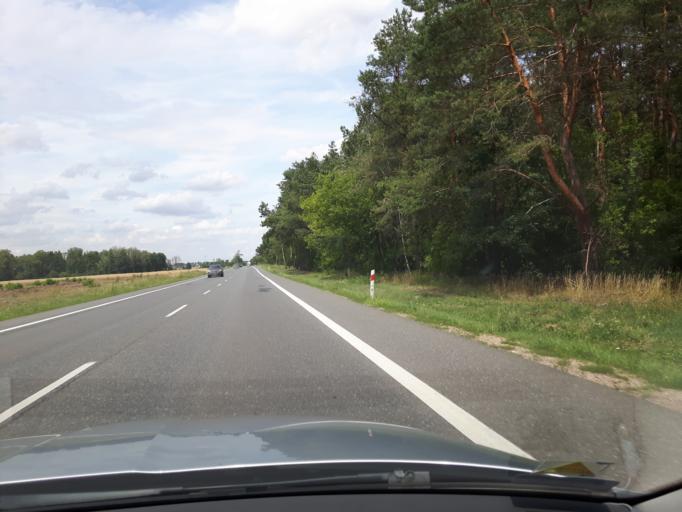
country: PL
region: Masovian Voivodeship
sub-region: Powiat mlawski
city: Strzegowo
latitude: 52.9218
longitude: 20.2862
